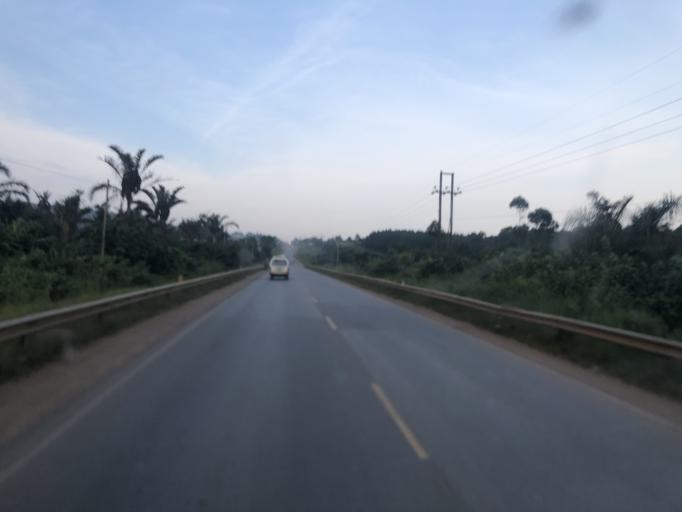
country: UG
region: Central Region
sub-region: Mpigi District
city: Mpigi
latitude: 0.2420
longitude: 32.3583
